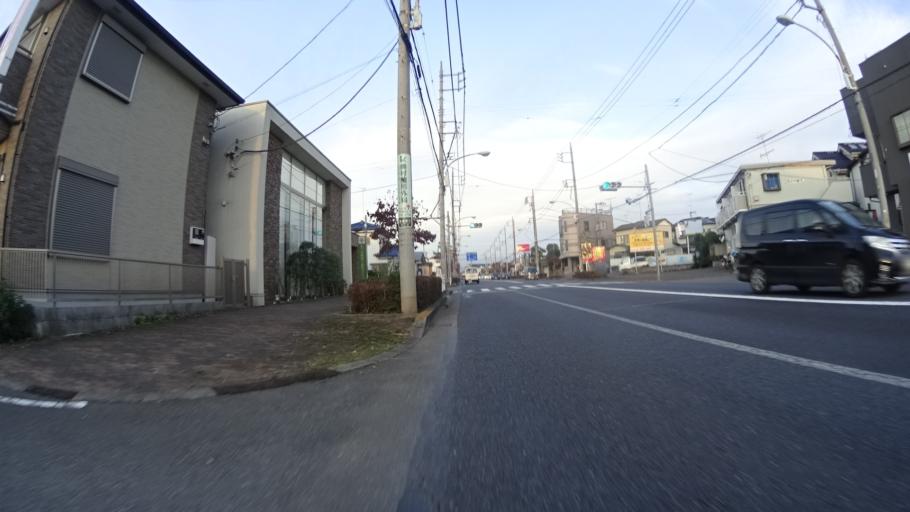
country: JP
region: Tokyo
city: Fussa
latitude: 35.7225
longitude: 139.3061
